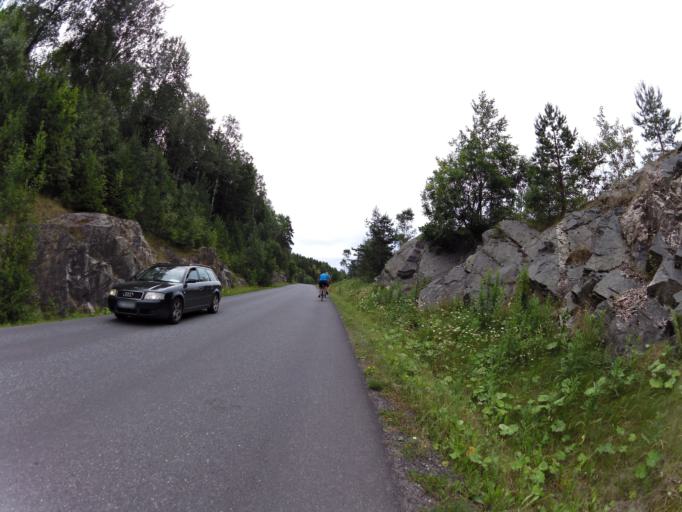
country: NO
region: Akershus
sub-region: As
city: As
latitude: 59.6914
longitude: 10.7343
